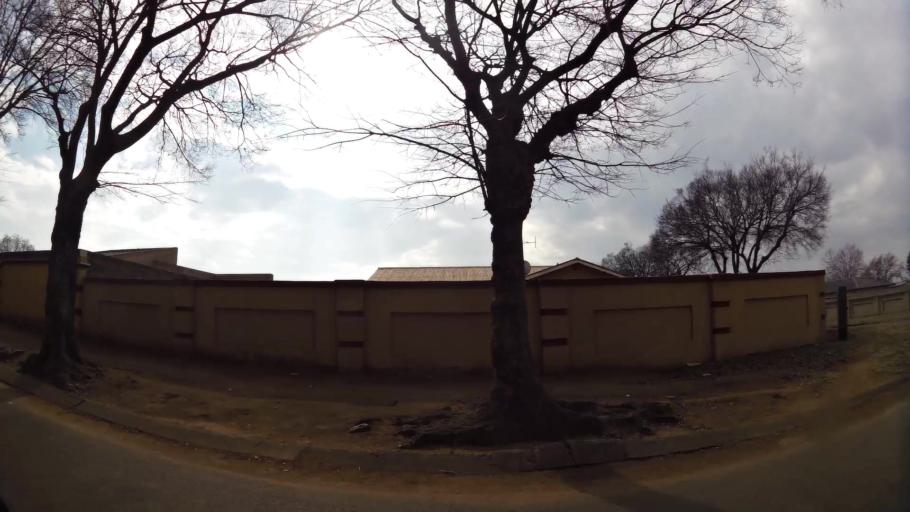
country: ZA
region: Gauteng
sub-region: Sedibeng District Municipality
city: Vanderbijlpark
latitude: -26.6790
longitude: 27.8348
